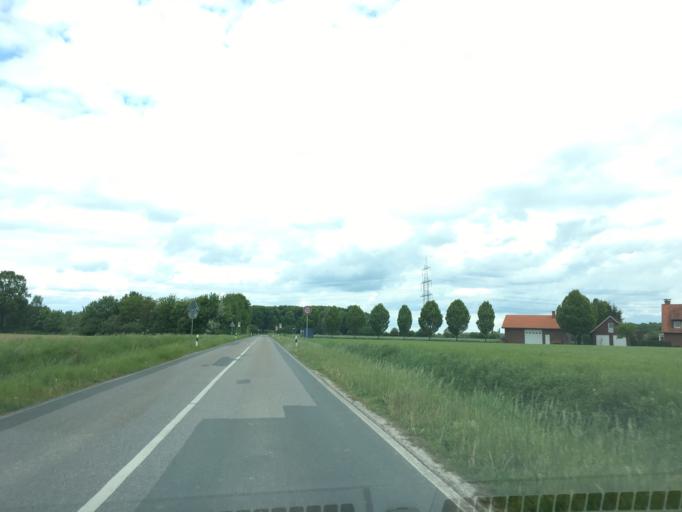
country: DE
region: North Rhine-Westphalia
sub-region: Regierungsbezirk Munster
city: Havixbeck
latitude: 51.9453
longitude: 7.4917
